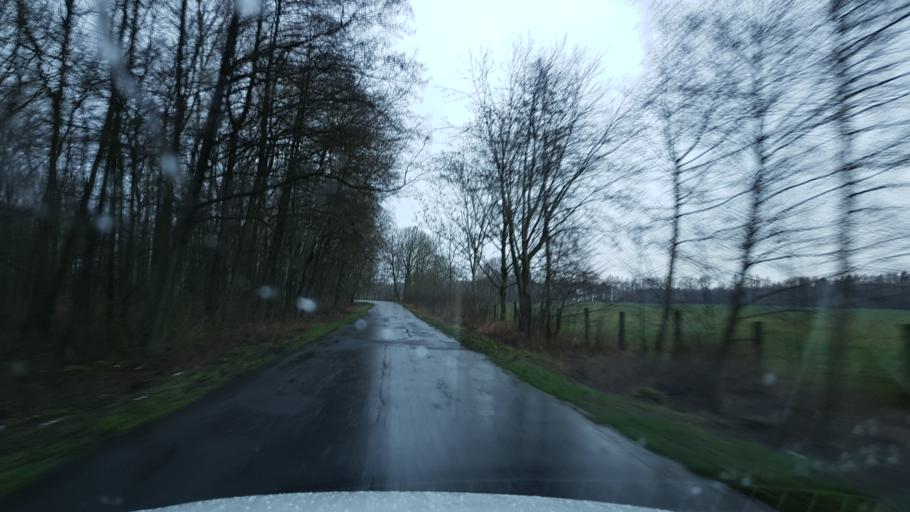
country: PL
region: West Pomeranian Voivodeship
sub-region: Powiat goleniowski
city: Nowogard
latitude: 53.5847
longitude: 15.1134
